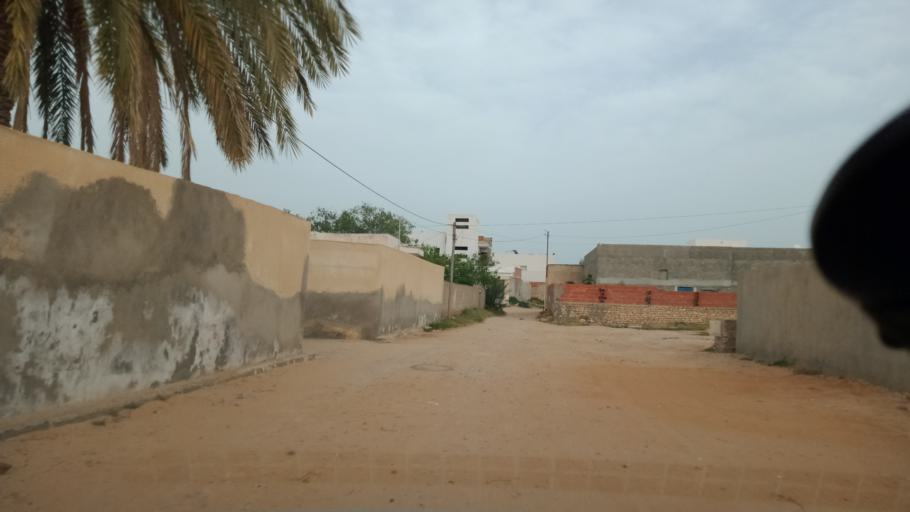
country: TN
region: Safaqis
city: Al Qarmadah
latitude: 34.7897
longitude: 10.7671
